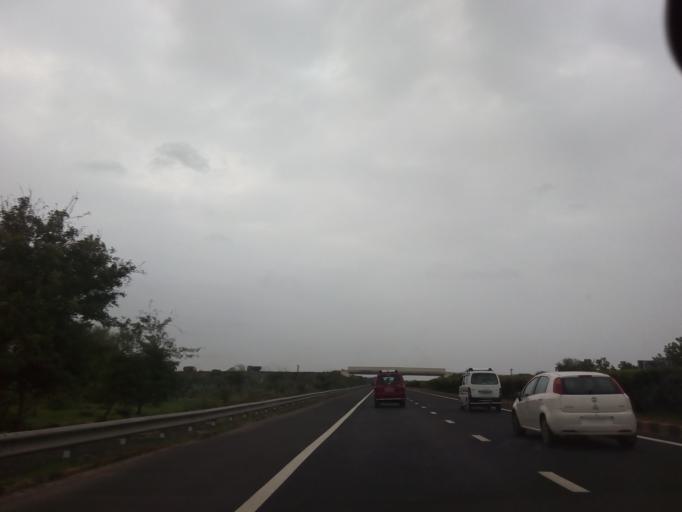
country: IN
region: Gujarat
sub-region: Kheda
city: Mahemdavad
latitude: 22.8256
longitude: 72.8279
